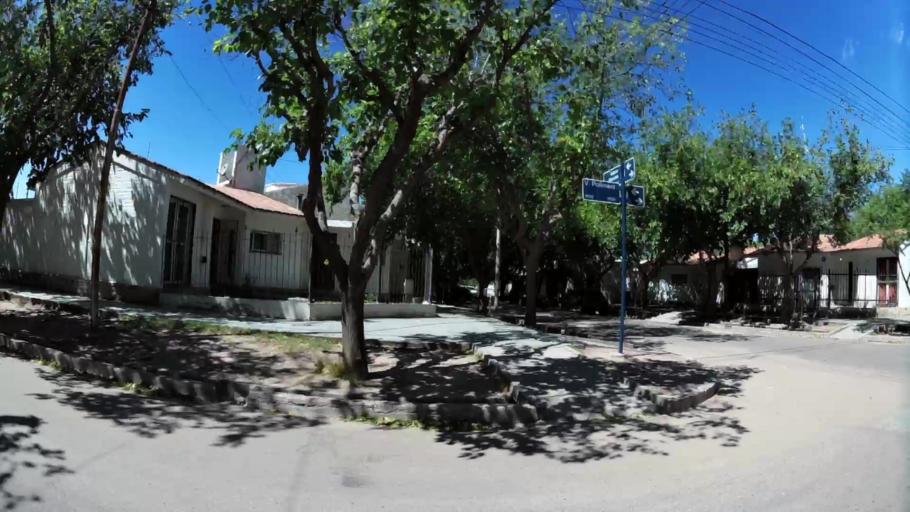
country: AR
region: Mendoza
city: Las Heras
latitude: -32.8509
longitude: -68.8490
